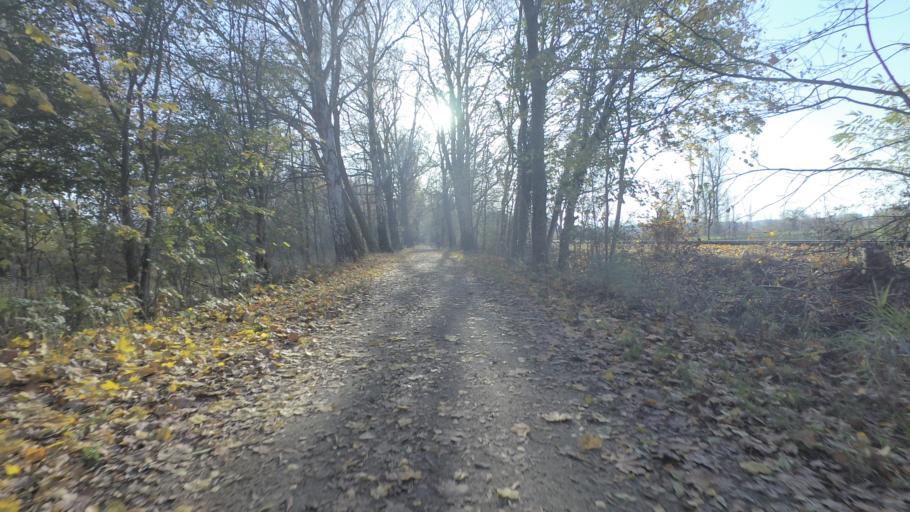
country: DE
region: Brandenburg
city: Am Mellensee
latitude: 52.1996
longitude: 13.4155
